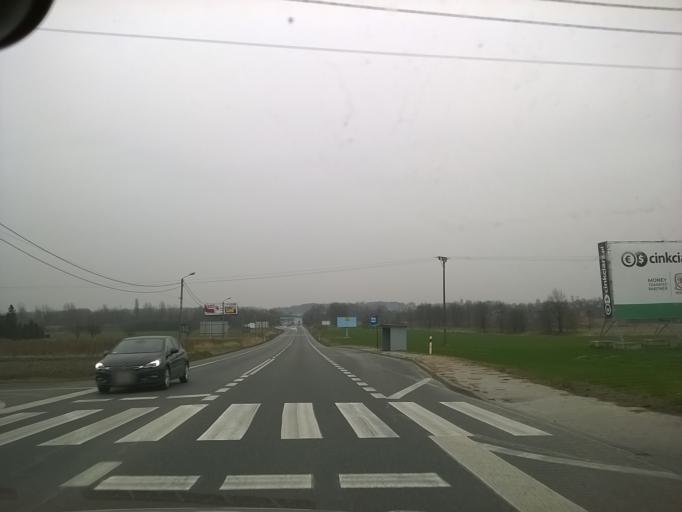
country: PL
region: Silesian Voivodeship
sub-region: Powiat gliwicki
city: Przyszowice
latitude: 50.2562
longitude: 18.7320
